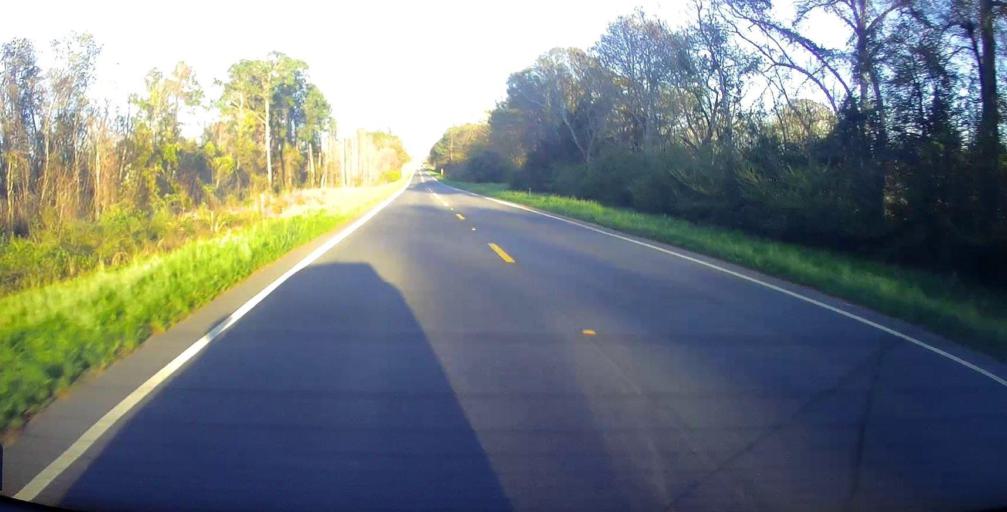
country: US
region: Georgia
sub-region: Wilcox County
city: Rochelle
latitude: 31.9499
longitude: -83.4823
